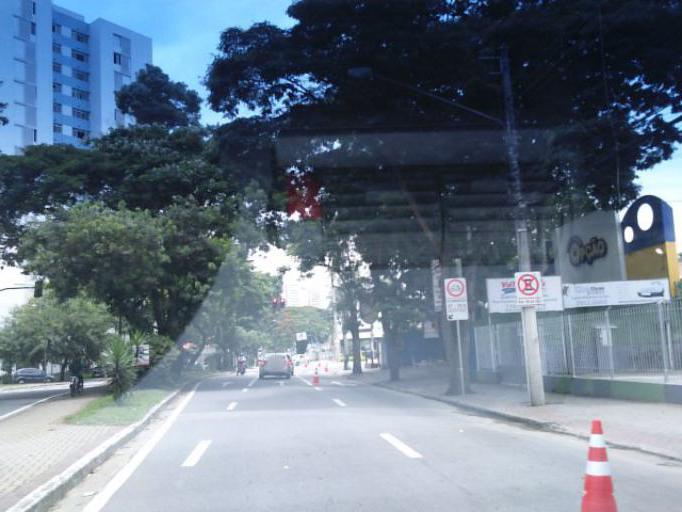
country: BR
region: Sao Paulo
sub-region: Sao Jose Dos Campos
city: Sao Jose dos Campos
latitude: -23.1923
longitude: -45.8929
